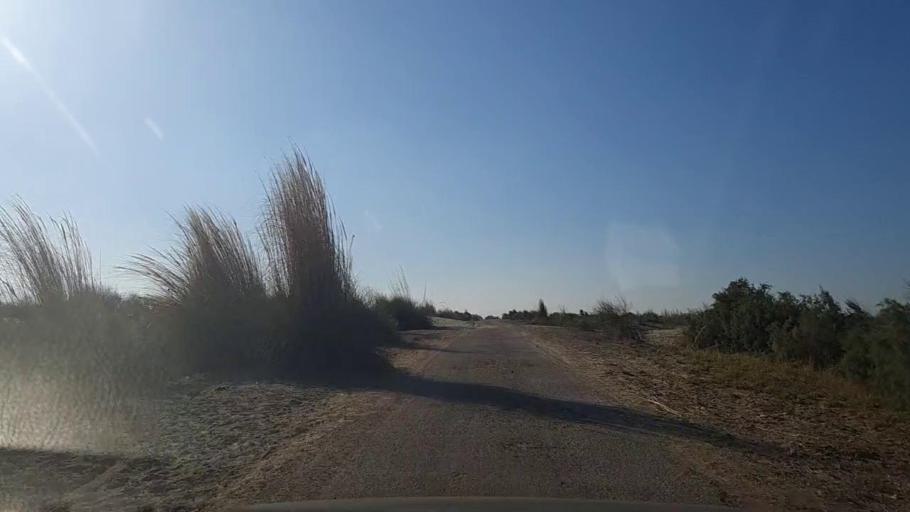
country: PK
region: Sindh
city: Khadro
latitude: 26.2412
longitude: 68.8836
